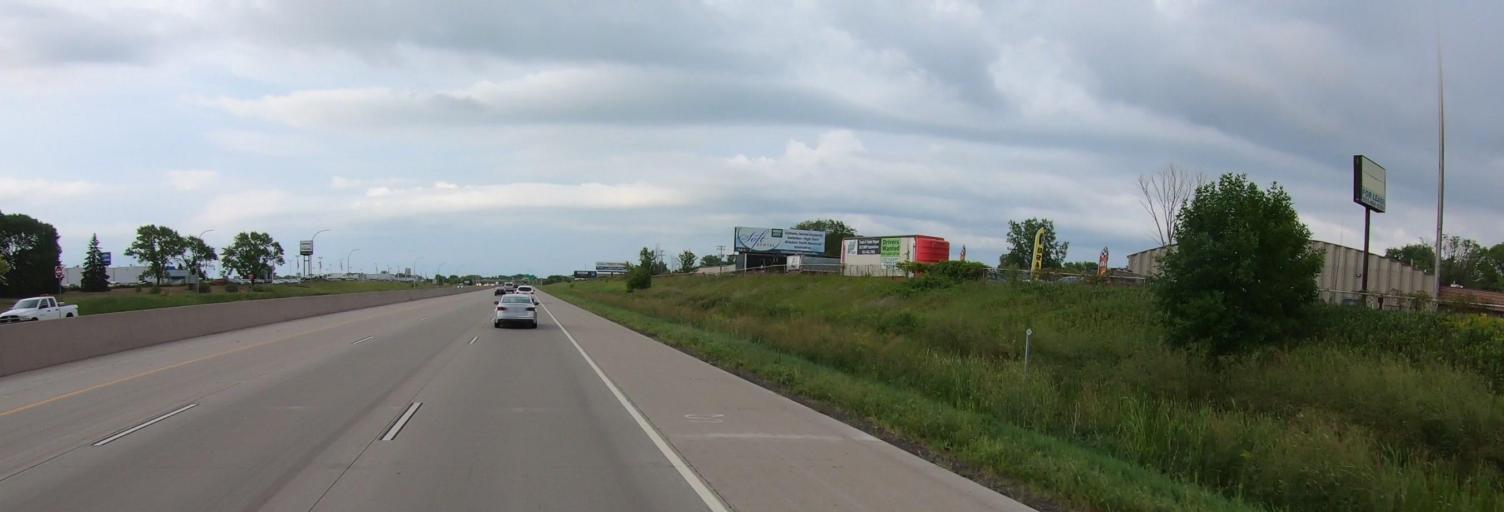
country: US
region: Minnesota
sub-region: Washington County
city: Forest Lake
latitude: 45.2709
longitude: -93.0072
